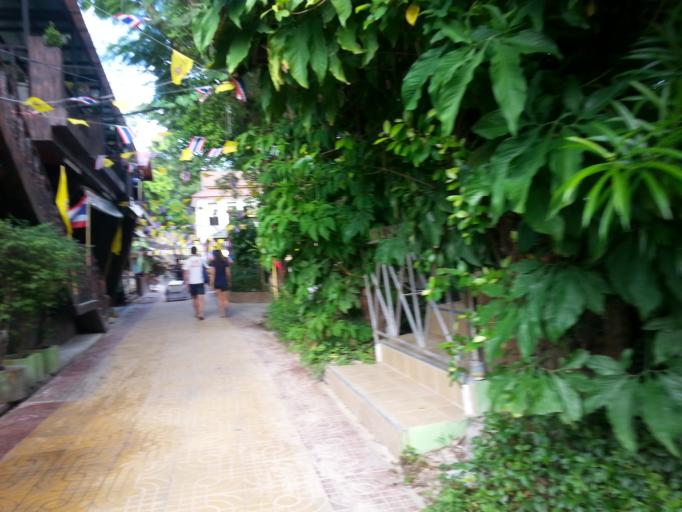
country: TH
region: Phangnga
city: Ban Phru Nai
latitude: 7.7380
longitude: 98.7734
